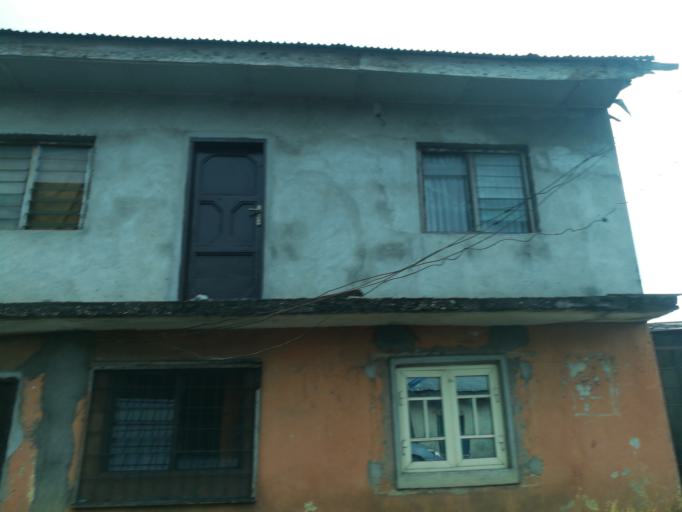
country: NG
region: Rivers
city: Port Harcourt
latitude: 4.8015
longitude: 6.9861
